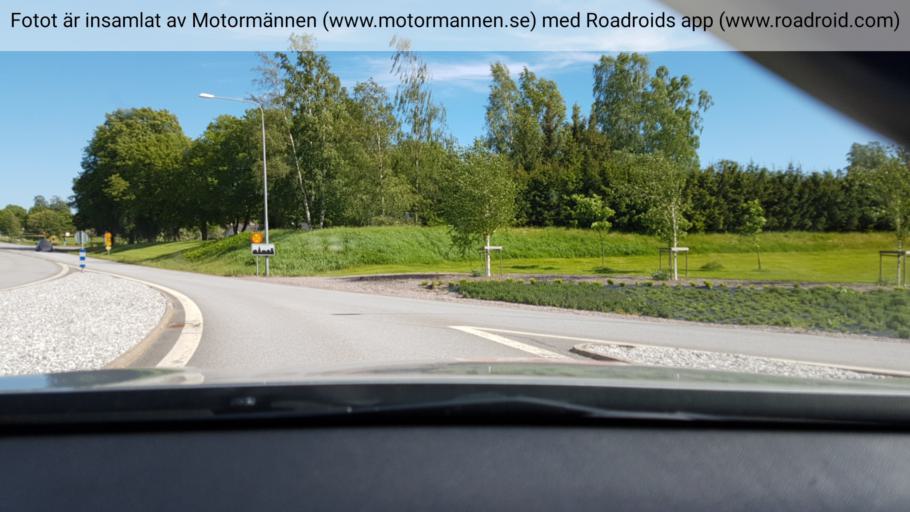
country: SE
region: Vaestra Goetaland
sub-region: Tibro Kommun
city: Tibro
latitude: 58.4267
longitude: 14.1429
